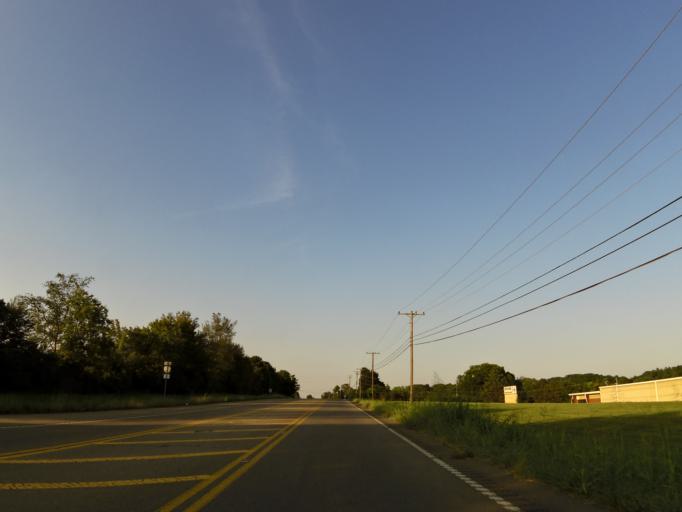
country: US
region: Tennessee
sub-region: McMinn County
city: Athens
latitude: 35.5198
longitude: -84.5424
